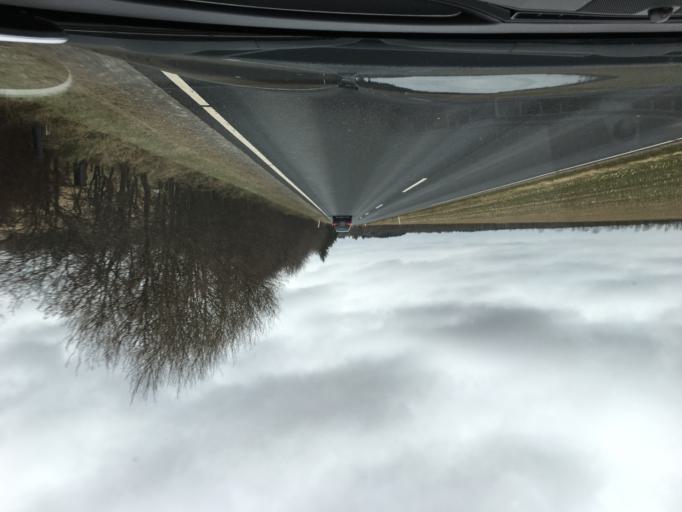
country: DK
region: South Denmark
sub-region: Varde Kommune
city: Varde
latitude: 55.5768
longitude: 8.5326
